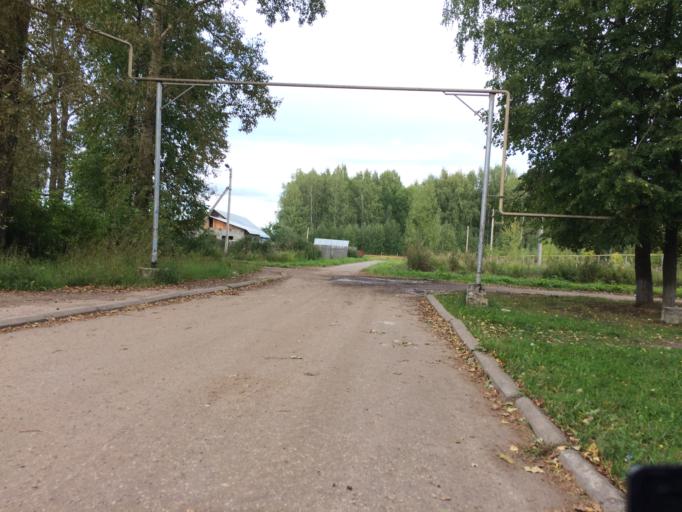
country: RU
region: Mariy-El
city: Yoshkar-Ola
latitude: 56.6570
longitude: 47.9835
